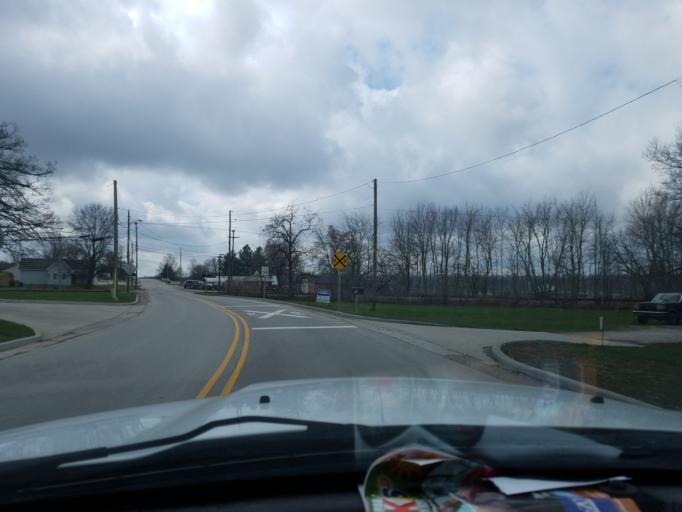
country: US
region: Indiana
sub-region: Vigo County
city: Seelyville
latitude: 39.3913
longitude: -87.3051
